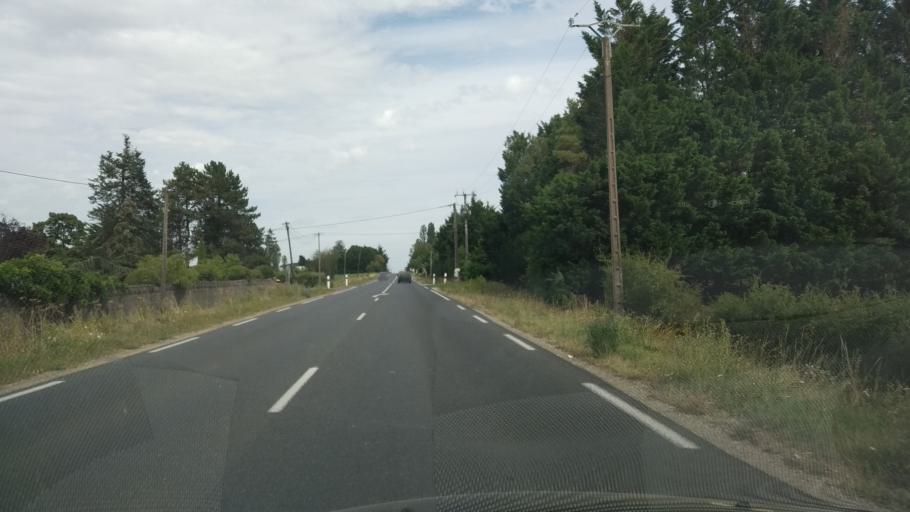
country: FR
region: Poitou-Charentes
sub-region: Departement de la Vienne
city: Mignaloux-Beauvoir
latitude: 46.5613
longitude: 0.4341
